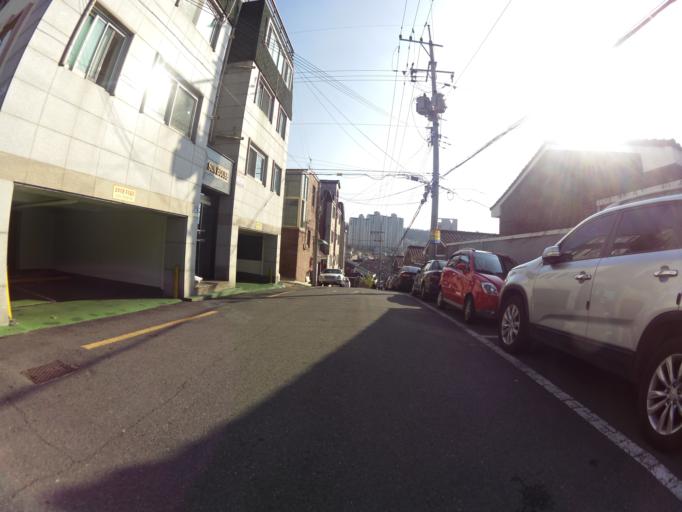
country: KR
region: Daegu
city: Daegu
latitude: 35.8614
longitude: 128.6419
